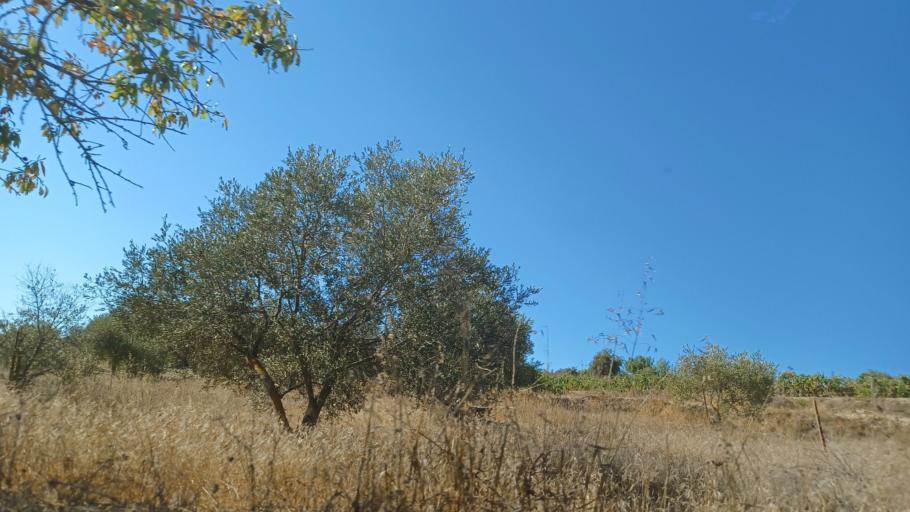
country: CY
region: Pafos
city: Mesogi
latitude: 34.8637
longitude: 32.5206
